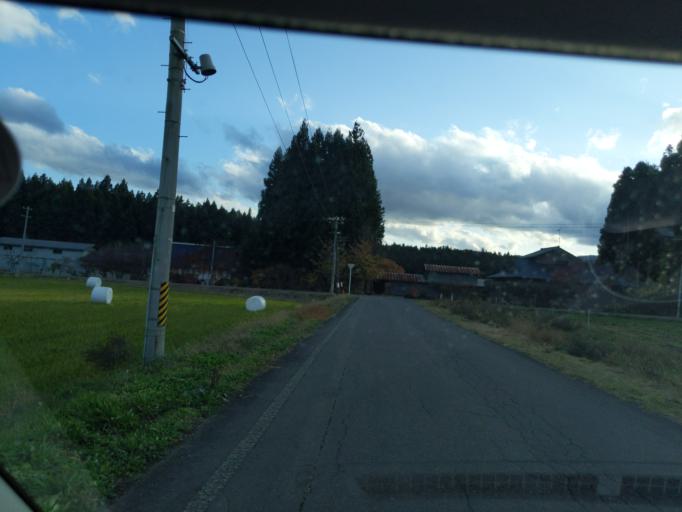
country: JP
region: Iwate
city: Mizusawa
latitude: 39.1014
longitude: 140.9974
